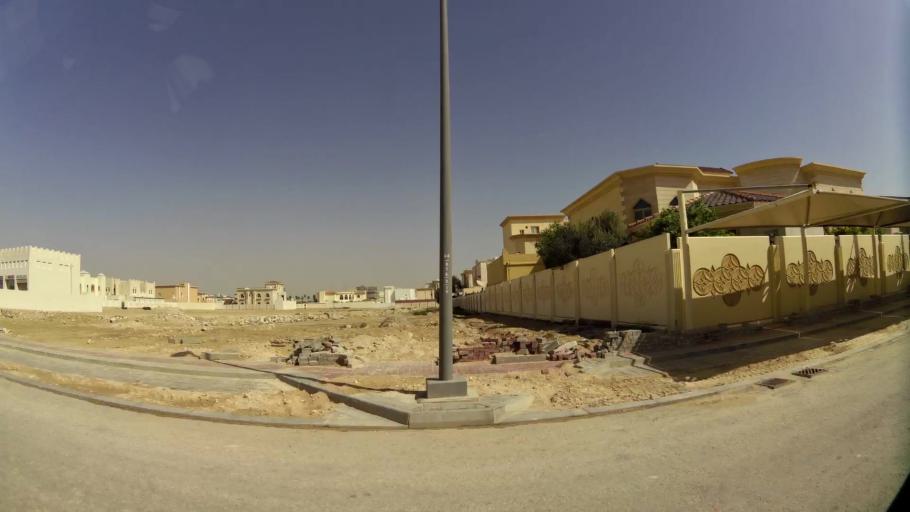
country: QA
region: Baladiyat ad Dawhah
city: Doha
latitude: 25.3605
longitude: 51.4975
